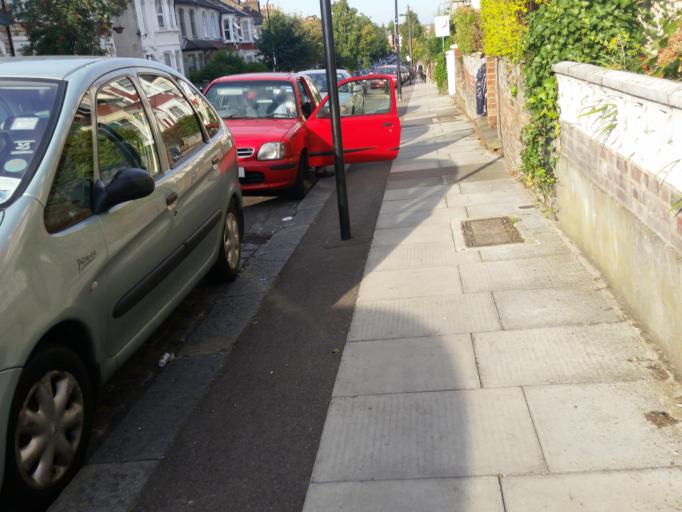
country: GB
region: England
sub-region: Greater London
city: Harringay
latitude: 51.5847
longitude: -0.1041
